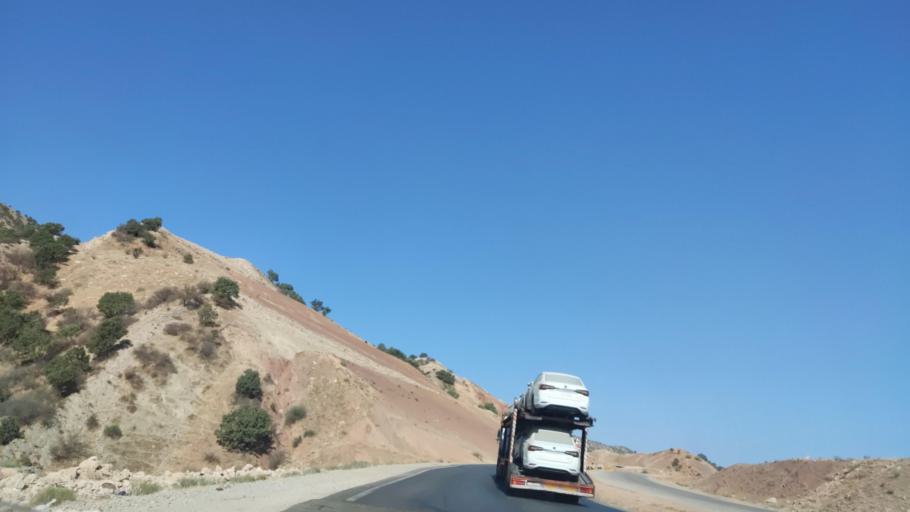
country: IQ
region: Arbil
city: Shaqlawah
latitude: 36.4331
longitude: 44.3042
